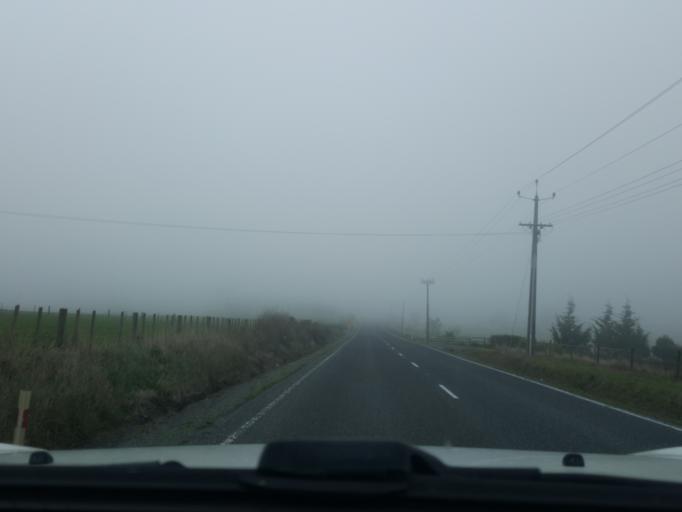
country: NZ
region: Auckland
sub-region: Auckland
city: Pukekohe East
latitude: -37.3008
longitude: 175.0264
